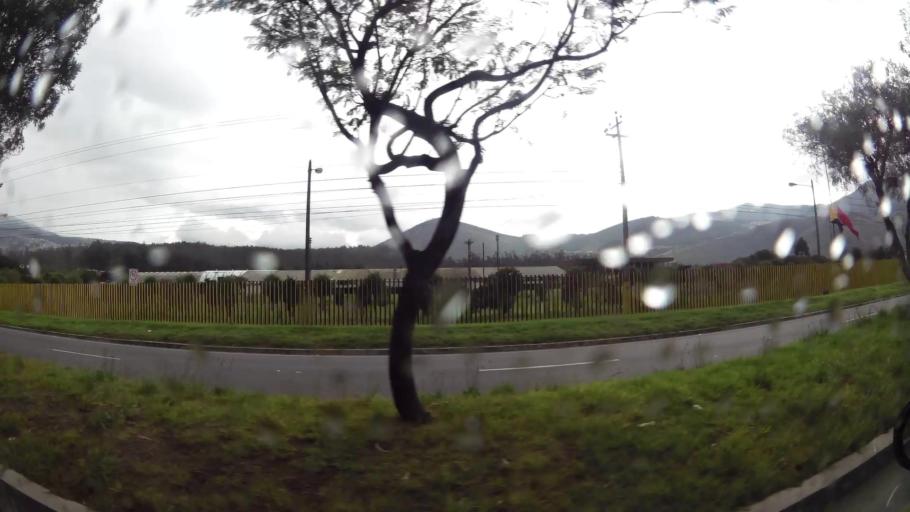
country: EC
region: Pichincha
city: Quito
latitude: -0.0870
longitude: -78.4857
